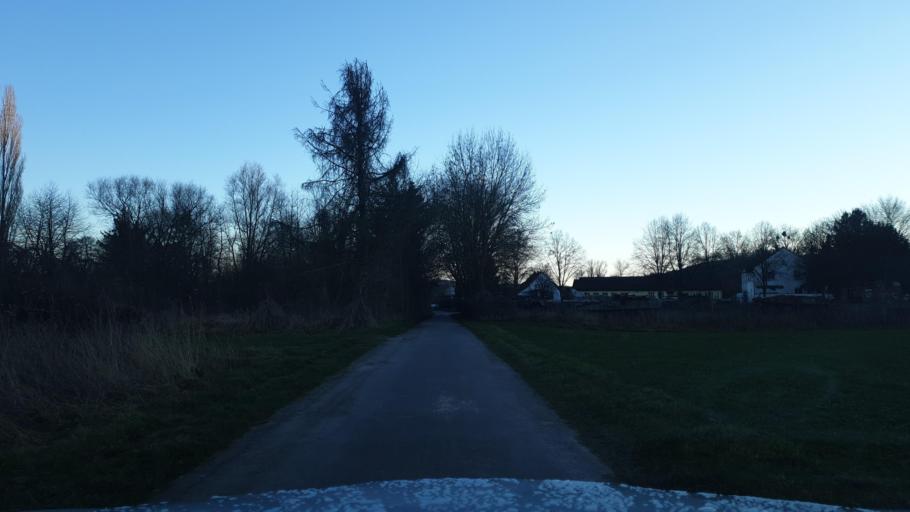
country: DE
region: North Rhine-Westphalia
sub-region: Regierungsbezirk Detmold
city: Vlotho
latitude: 52.2040
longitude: 8.8484
